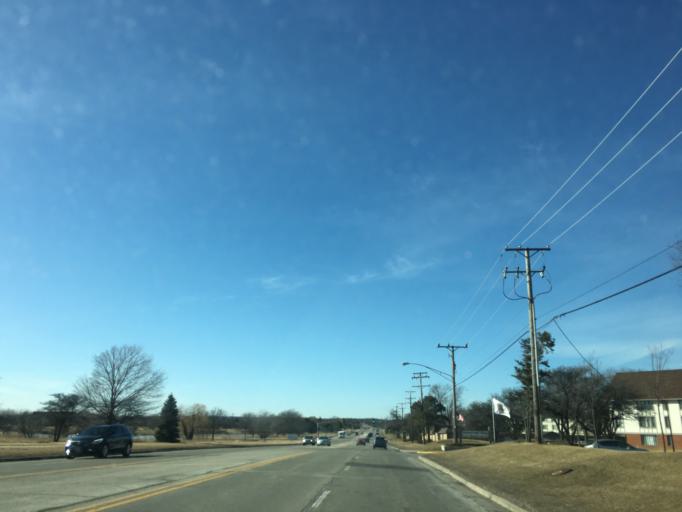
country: US
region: Illinois
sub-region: Cook County
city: Rolling Meadows
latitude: 42.0696
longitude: -88.0473
